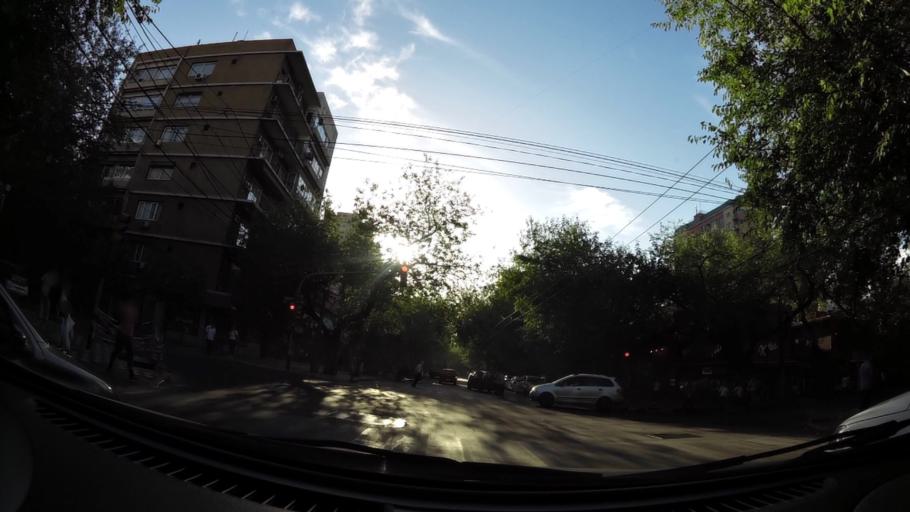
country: AR
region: Mendoza
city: Mendoza
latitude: -32.8943
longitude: -68.8442
